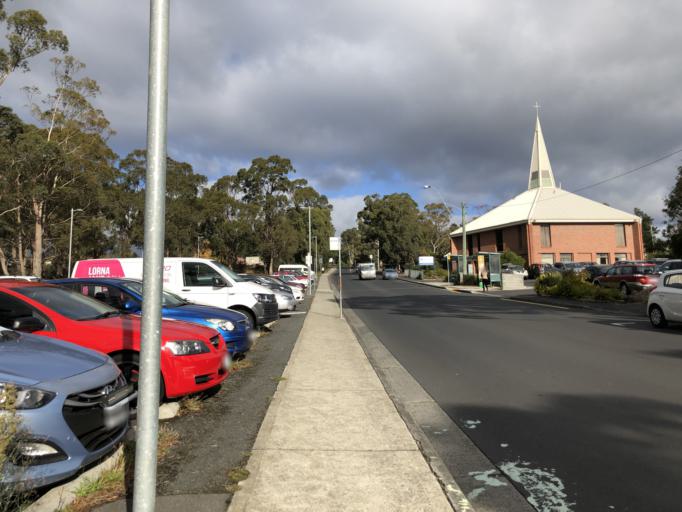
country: AU
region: Tasmania
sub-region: Kingborough
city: Kingston
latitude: -42.9781
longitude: 147.3067
